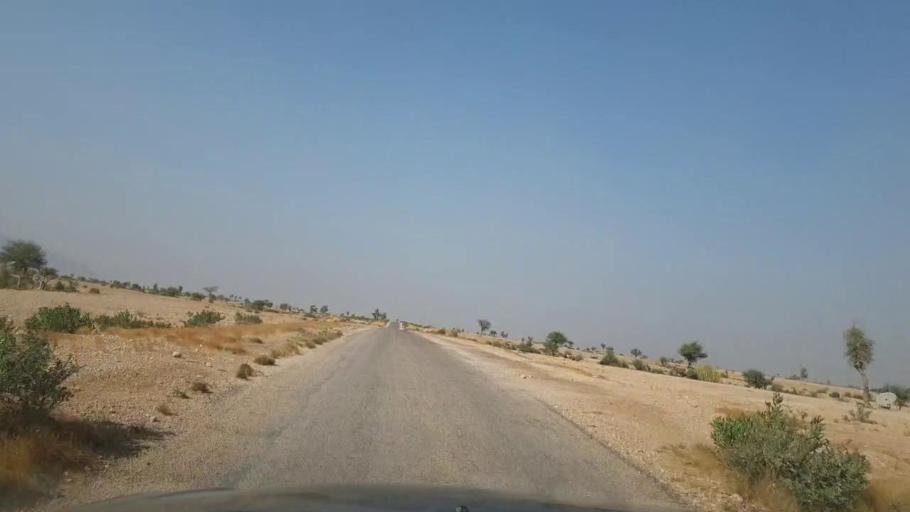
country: PK
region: Sindh
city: Jamshoro
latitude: 25.5983
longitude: 67.8167
